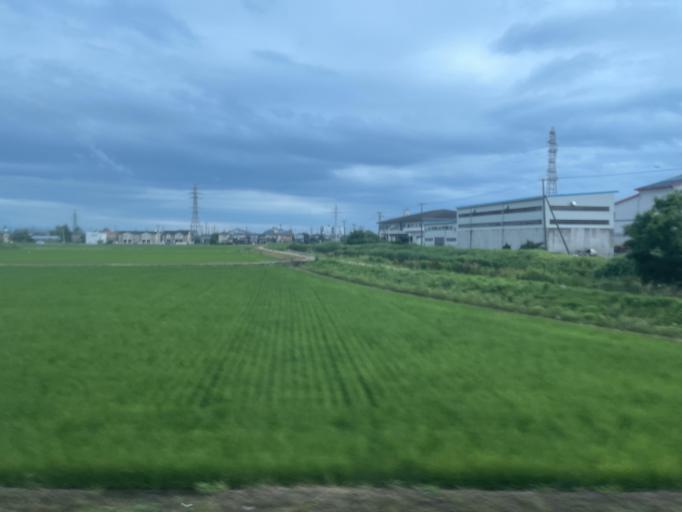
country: JP
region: Niigata
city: Yoshida-kasugacho
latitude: 37.6830
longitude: 138.9033
